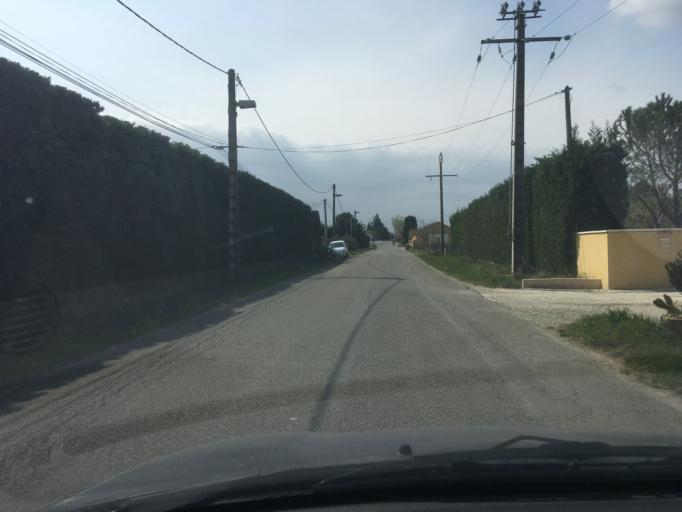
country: FR
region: Provence-Alpes-Cote d'Azur
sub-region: Departement du Vaucluse
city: Sarrians
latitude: 44.0835
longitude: 4.9805
